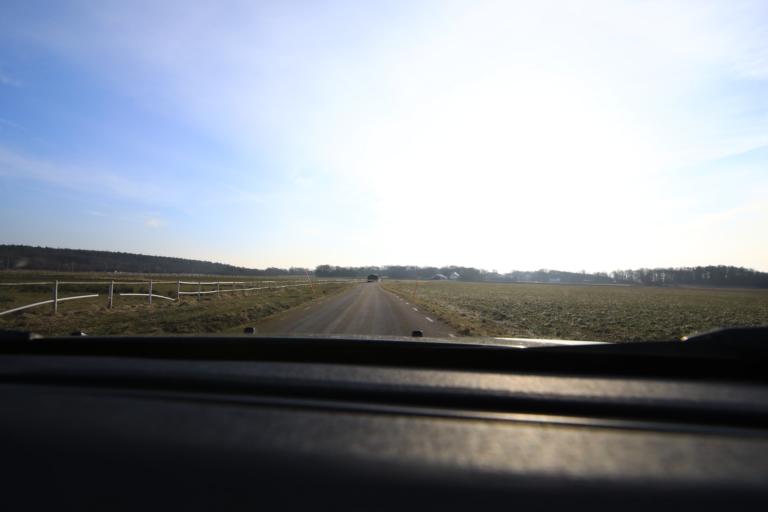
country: SE
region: Halland
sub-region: Varbergs Kommun
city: Varberg
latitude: 57.1991
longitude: 12.2182
